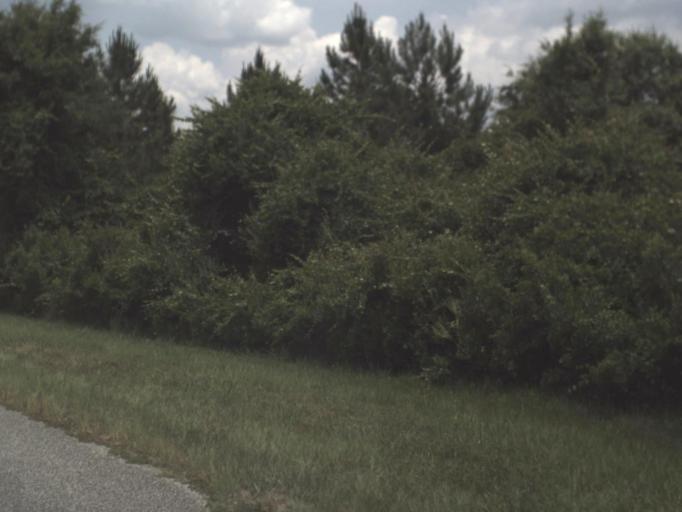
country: US
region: Florida
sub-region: Putnam County
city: Palatka
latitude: 29.5743
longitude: -81.7216
